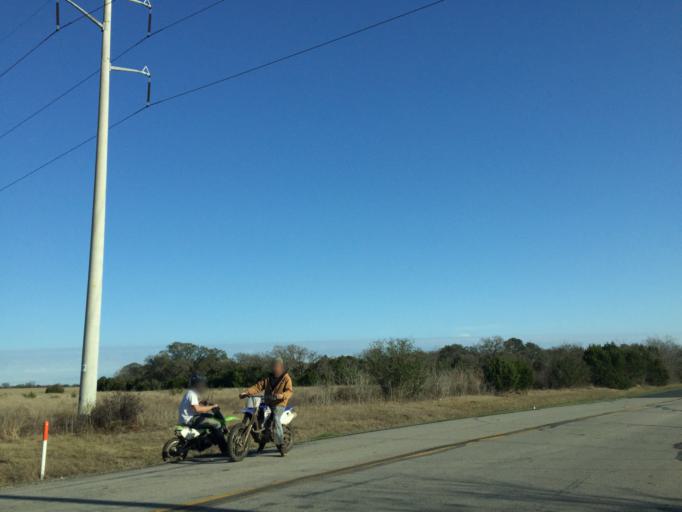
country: US
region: Texas
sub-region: Williamson County
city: Florence
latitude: 30.7805
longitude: -97.7927
